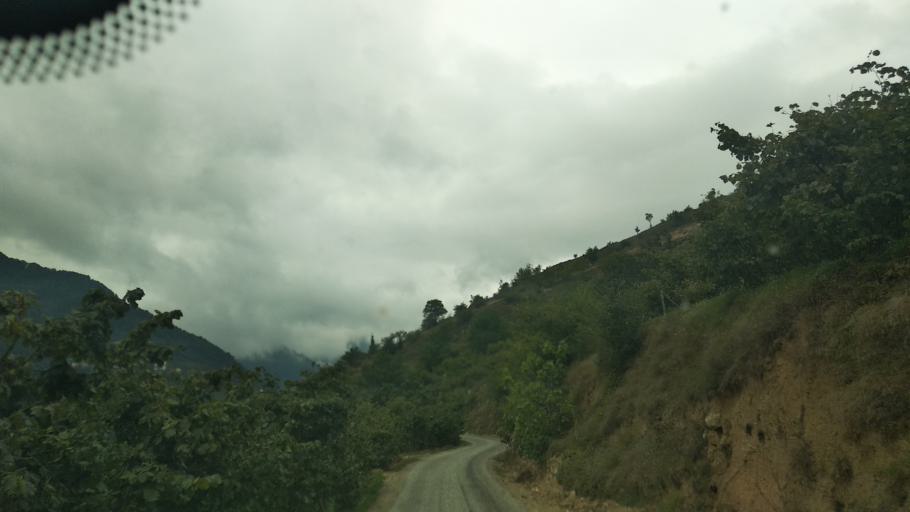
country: TR
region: Giresun
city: Dogankent
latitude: 40.7414
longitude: 38.9930
